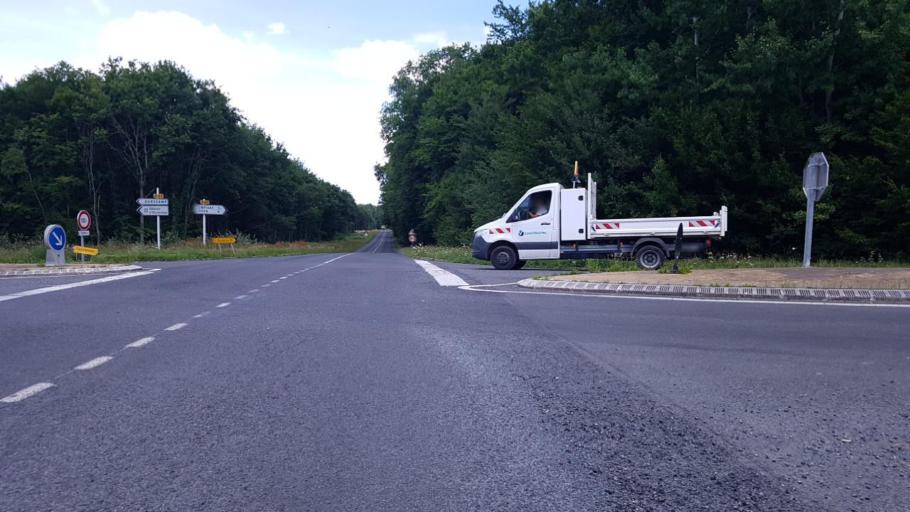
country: FR
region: Picardie
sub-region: Departement de l'Oise
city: Chiry-Ourscamp
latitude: 49.5291
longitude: 2.9843
